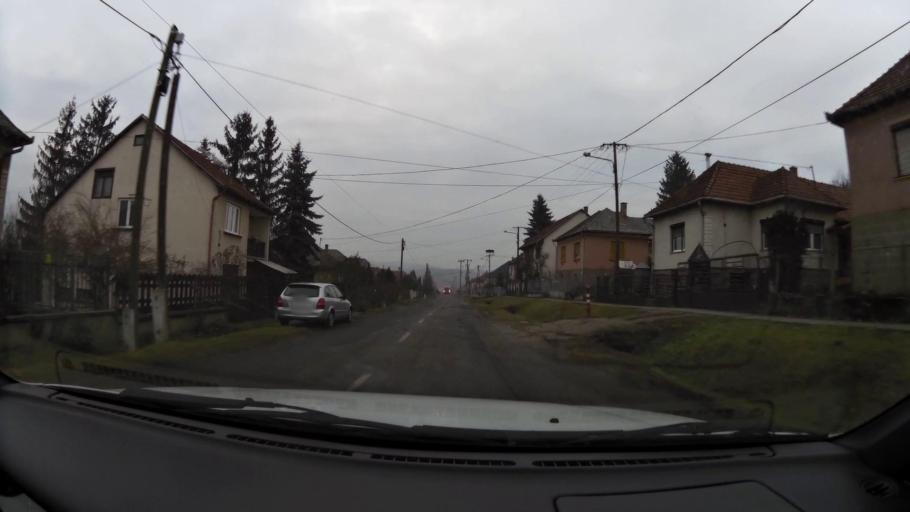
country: HU
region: Borsod-Abauj-Zemplen
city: Rudabanya
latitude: 48.4041
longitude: 20.6320
